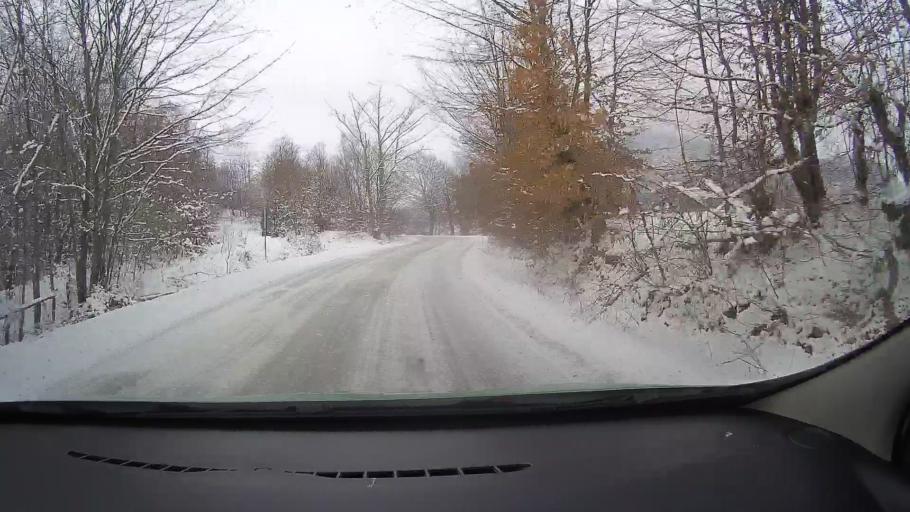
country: RO
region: Alba
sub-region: Comuna Almasu Mare
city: Almasu Mare
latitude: 46.0949
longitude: 23.1658
